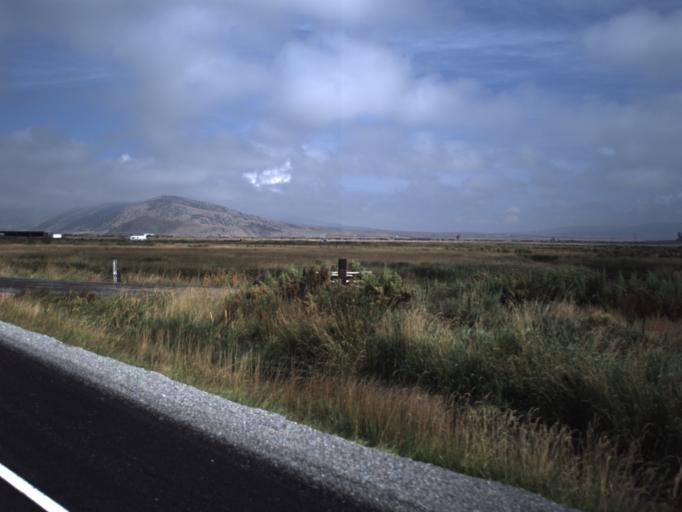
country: US
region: Utah
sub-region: Rich County
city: Randolph
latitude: 41.5023
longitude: -111.1236
